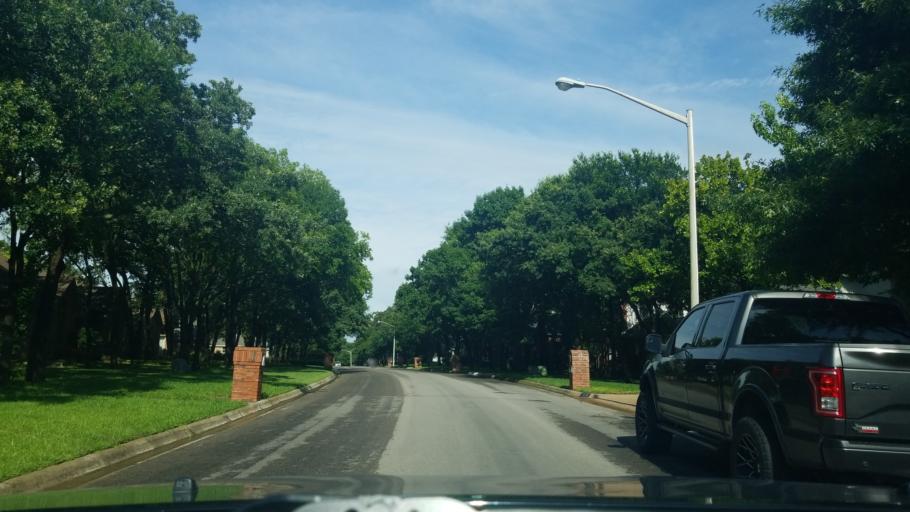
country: US
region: Texas
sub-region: Denton County
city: Denton
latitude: 33.1804
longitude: -97.1160
